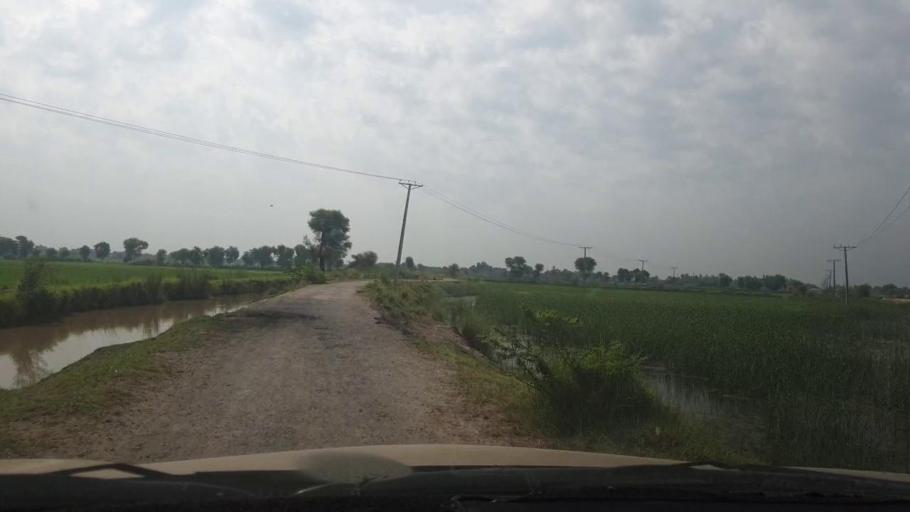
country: PK
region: Sindh
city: Larkana
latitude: 27.6427
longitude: 68.2015
